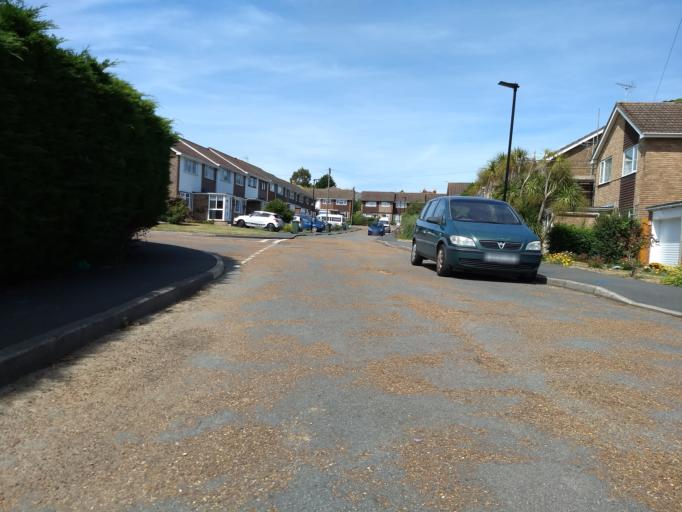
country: GB
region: England
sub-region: Isle of Wight
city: Ryde
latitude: 50.7161
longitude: -1.1718
